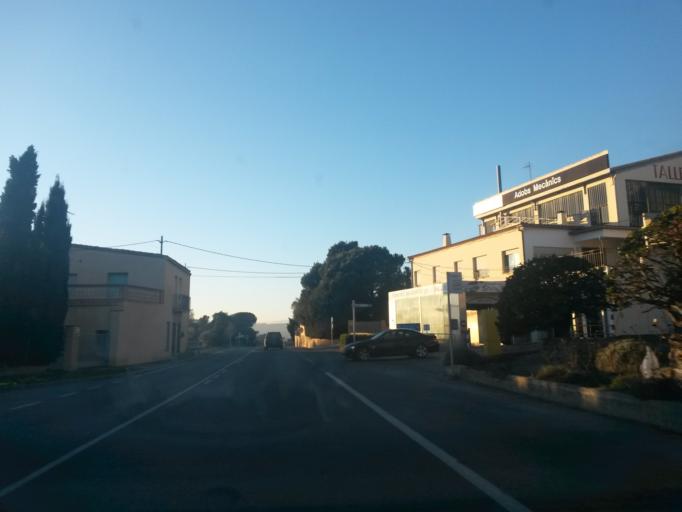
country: ES
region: Catalonia
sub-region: Provincia de Girona
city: Regencos
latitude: 41.9513
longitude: 3.1670
